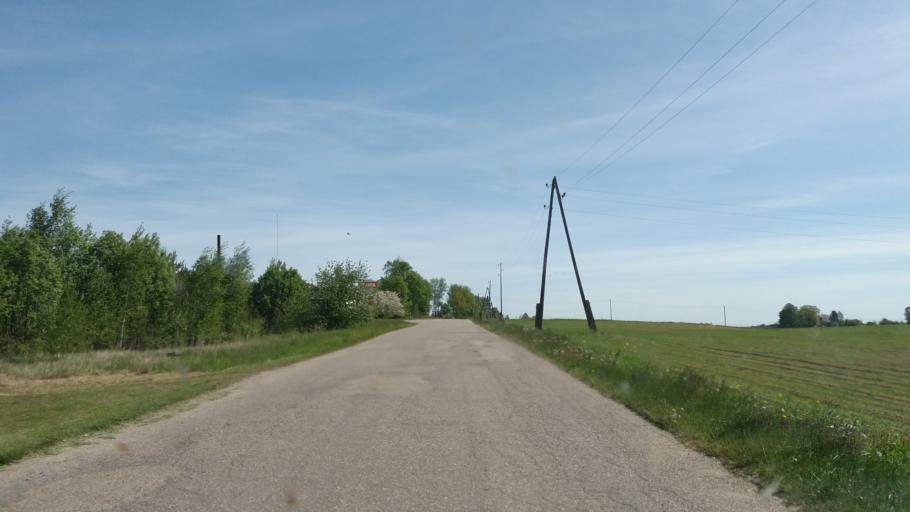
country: LV
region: Talsu Rajons
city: Sabile
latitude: 57.0527
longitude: 22.5893
